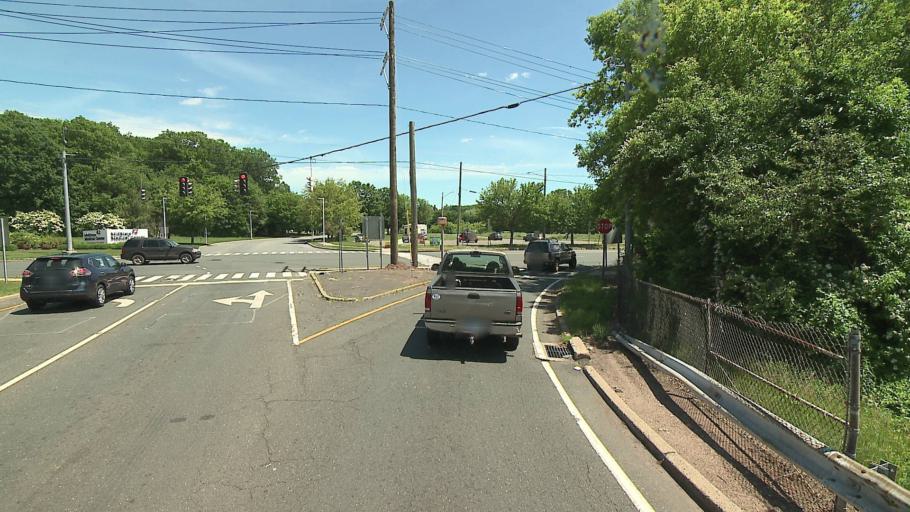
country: US
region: Connecticut
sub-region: New Haven County
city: Meriden
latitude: 41.5491
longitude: -72.8047
